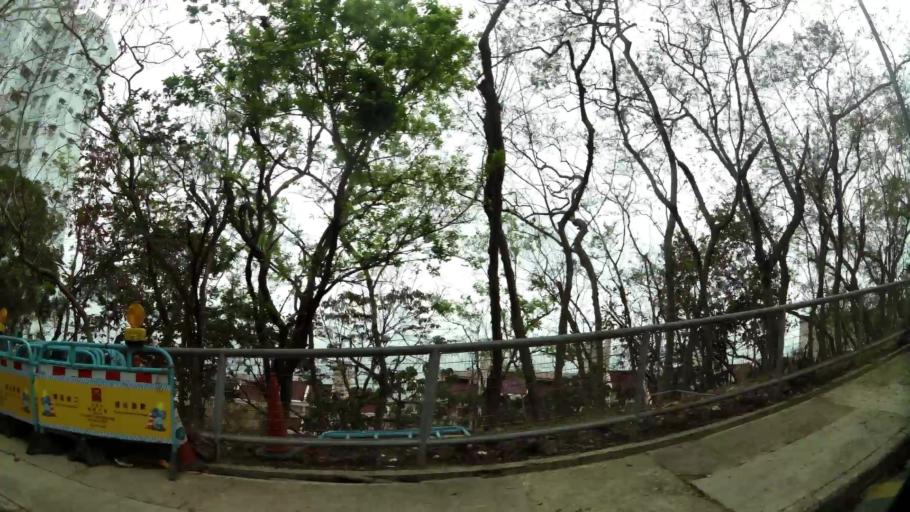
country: HK
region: Central and Western
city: Central
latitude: 22.2676
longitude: 114.1269
